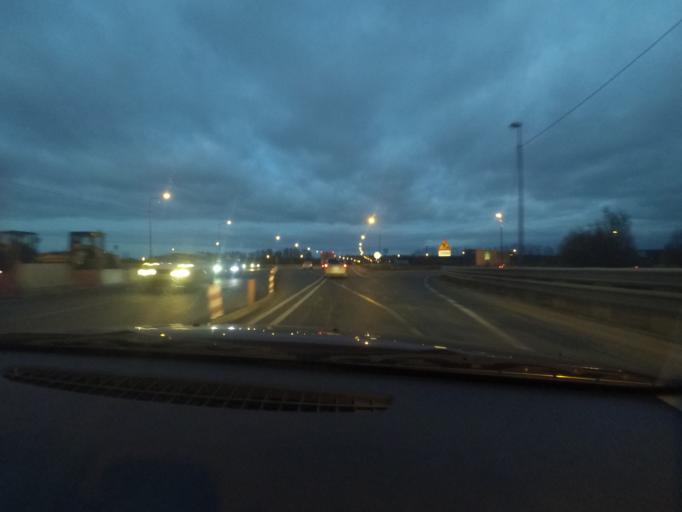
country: RU
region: Nizjnij Novgorod
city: Burevestnik
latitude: 56.1726
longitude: 43.7485
